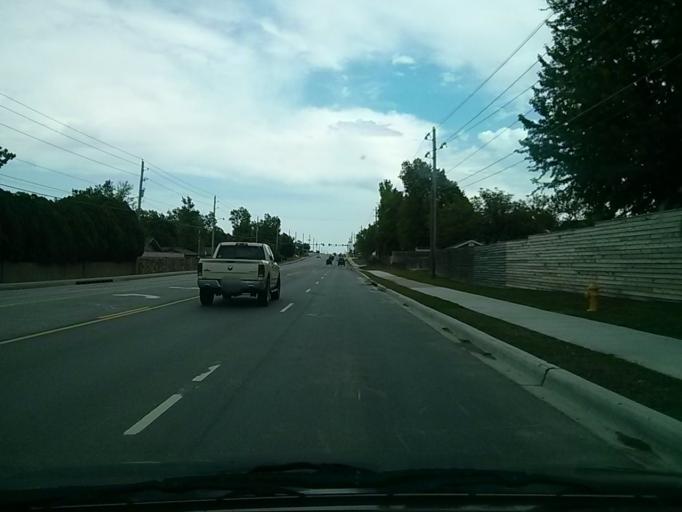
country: US
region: Oklahoma
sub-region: Tulsa County
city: Jenks
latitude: 36.0754
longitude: -95.8951
